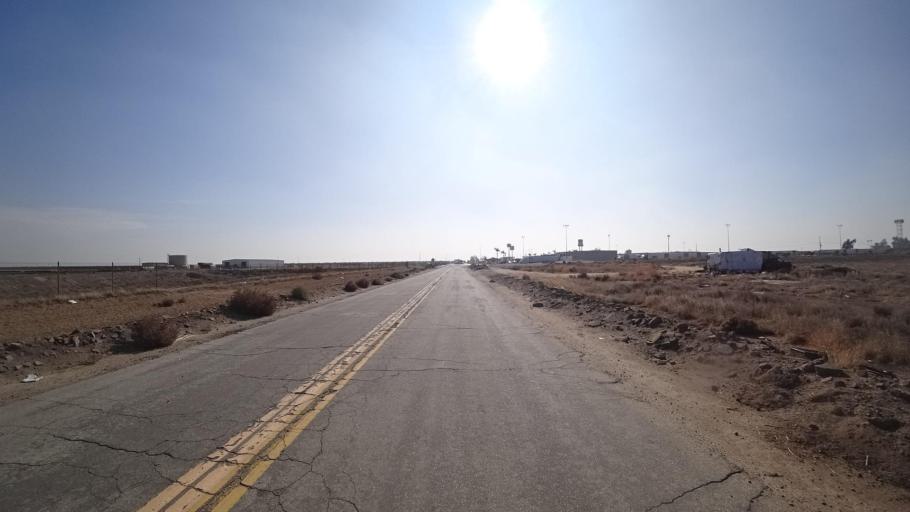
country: US
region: California
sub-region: Kern County
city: Shafter
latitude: 35.5345
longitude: -119.1868
